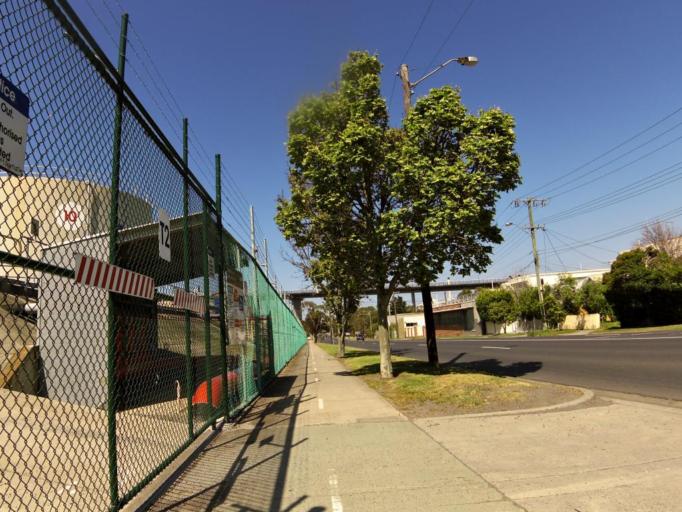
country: AU
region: Victoria
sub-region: Maribyrnong
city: Yarraville
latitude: -37.8228
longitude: 144.8958
